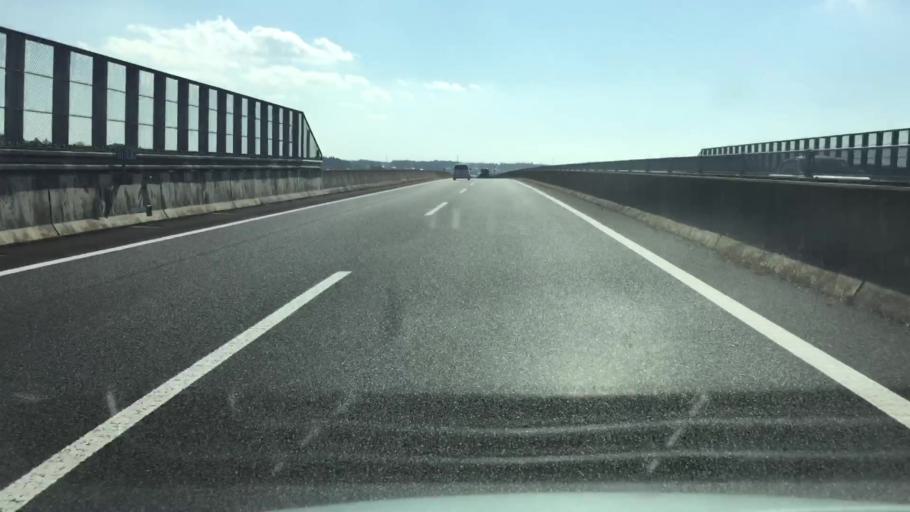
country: JP
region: Ibaraki
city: Tomobe
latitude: 36.3281
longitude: 140.2942
